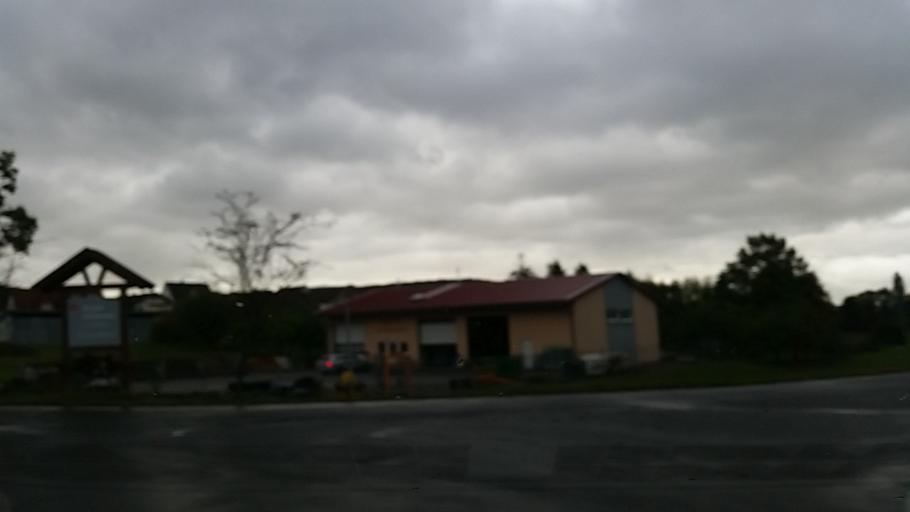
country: DE
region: Bavaria
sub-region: Regierungsbezirk Unterfranken
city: Gossenheim
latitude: 50.0186
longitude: 9.7787
